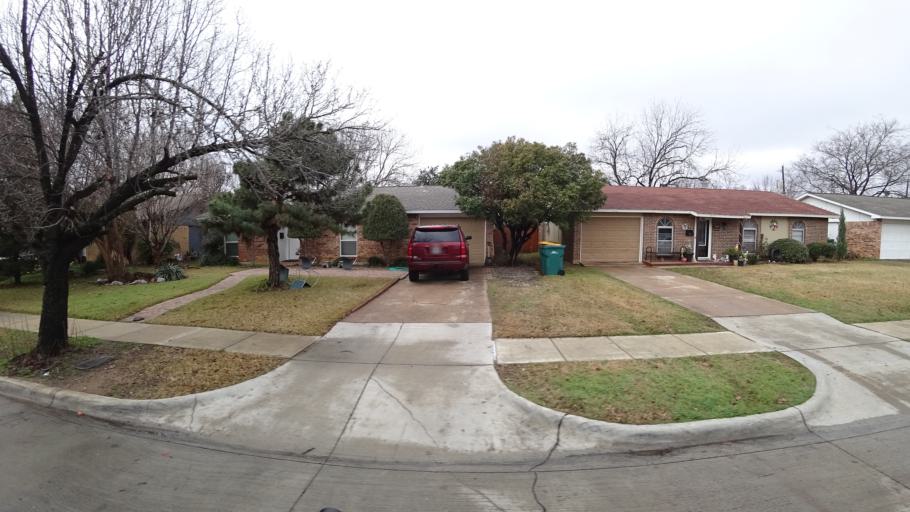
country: US
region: Texas
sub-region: Denton County
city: Lewisville
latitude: 33.0343
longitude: -97.0196
